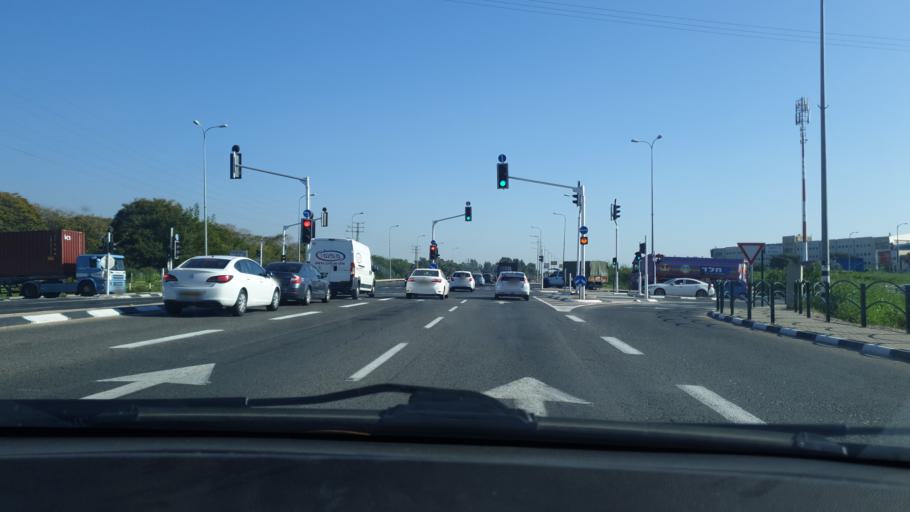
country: IL
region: Central District
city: Kefar Habad
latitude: 31.9601
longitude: 34.8513
